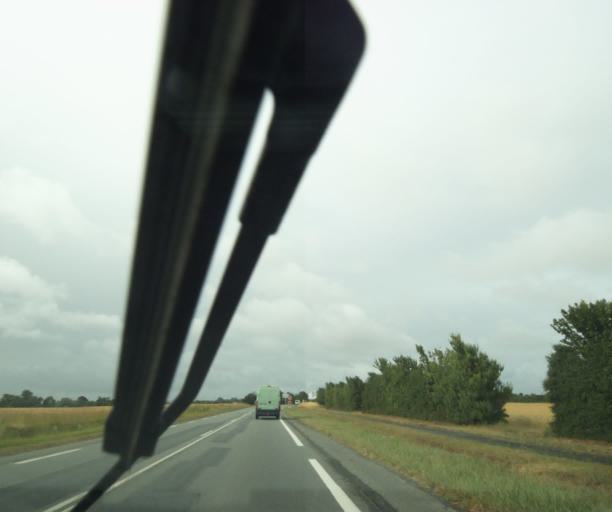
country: FR
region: Poitou-Charentes
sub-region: Departement de la Charente-Maritime
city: Lagord
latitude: 46.1945
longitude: -1.1410
